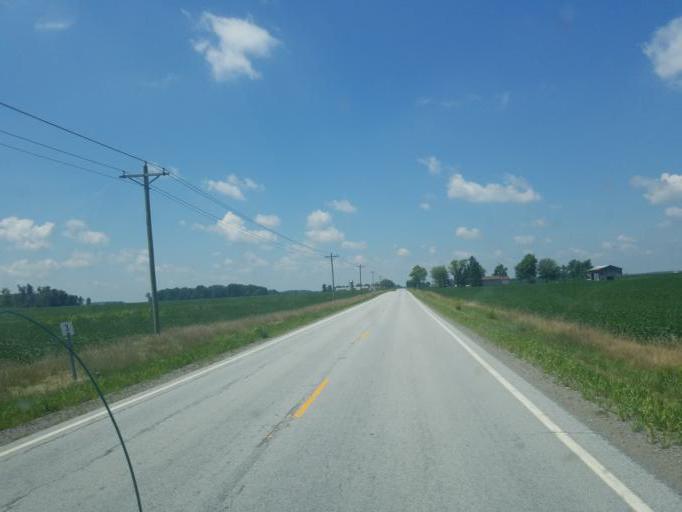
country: US
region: Ohio
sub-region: Allen County
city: Spencerville
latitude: 40.7141
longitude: -84.3990
